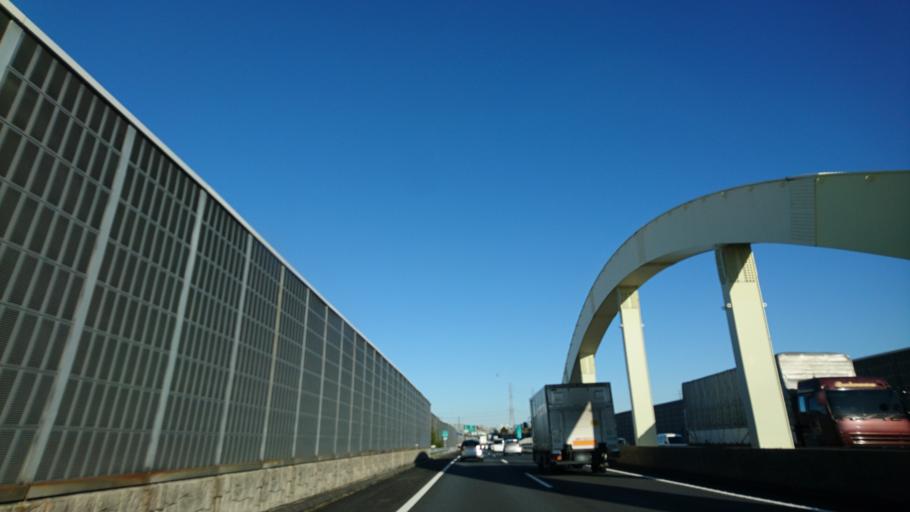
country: JP
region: Chiba
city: Chiba
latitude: 35.5533
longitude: 140.1399
